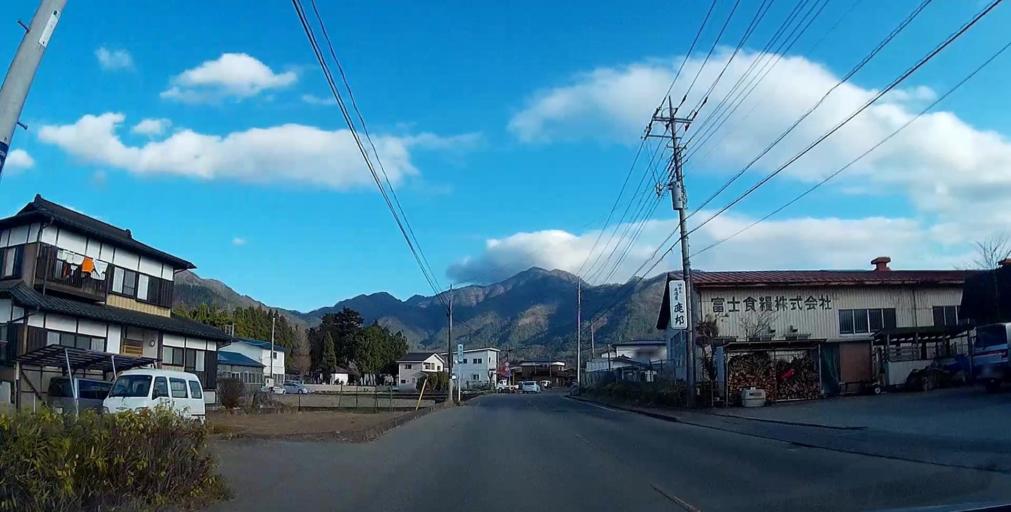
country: JP
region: Yamanashi
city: Fujikawaguchiko
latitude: 35.4952
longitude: 138.8216
